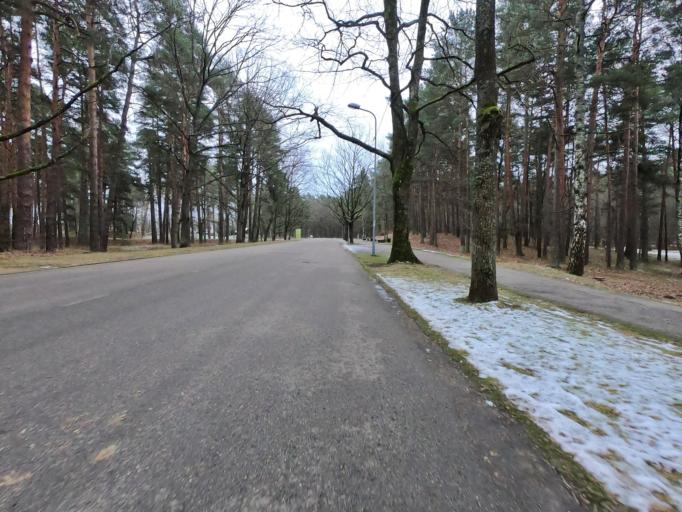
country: LV
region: Riga
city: Jaunciems
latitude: 57.0121
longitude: 24.1545
